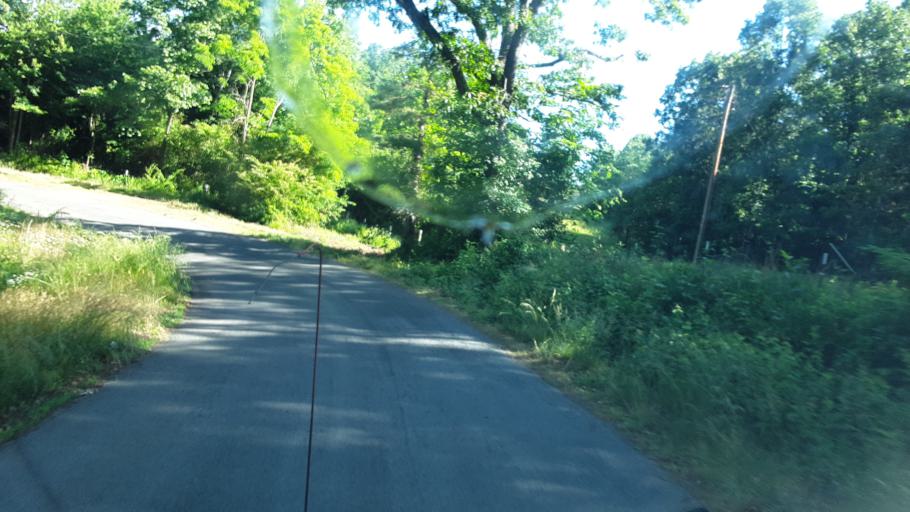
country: US
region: Virginia
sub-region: Pittsylvania County
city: Chatham
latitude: 36.8400
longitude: -79.3997
